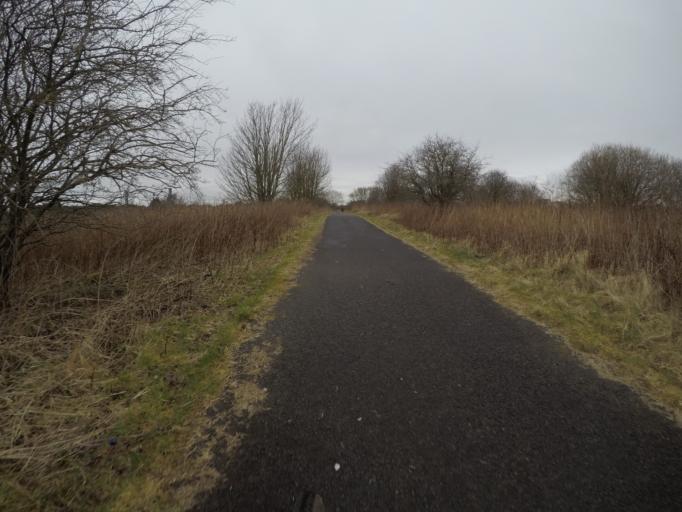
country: GB
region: Scotland
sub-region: North Ayrshire
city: Irvine
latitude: 55.6274
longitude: -4.6855
